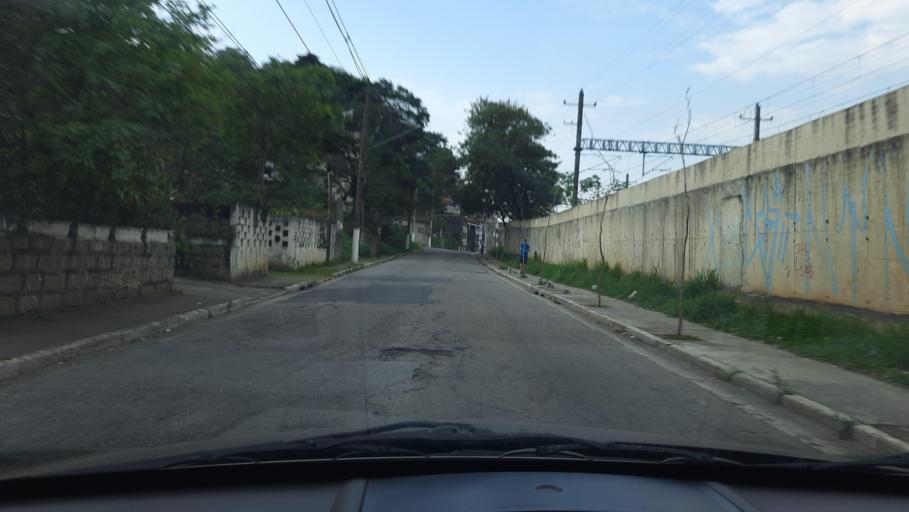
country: BR
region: Sao Paulo
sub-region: Caieiras
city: Caieiras
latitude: -23.4516
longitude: -46.7427
